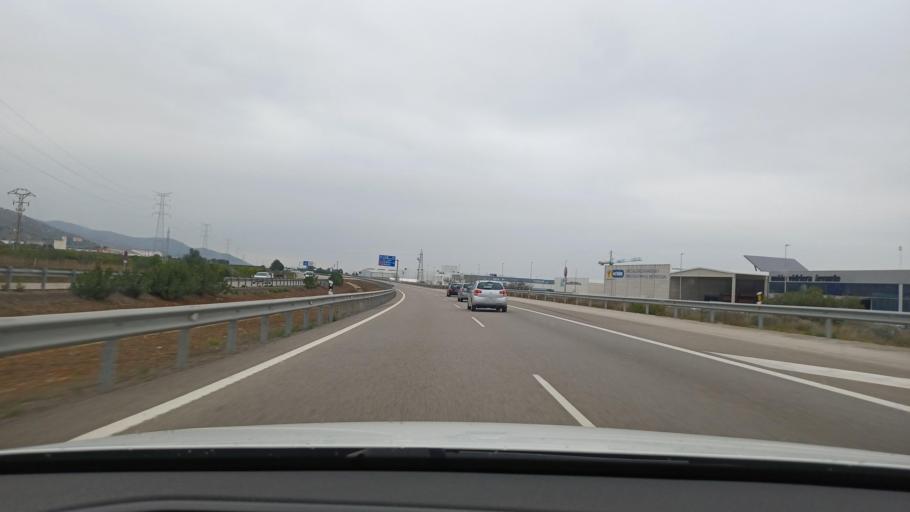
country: ES
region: Valencia
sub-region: Provincia de Castello
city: Chilches
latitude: 39.8094
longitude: -0.2169
